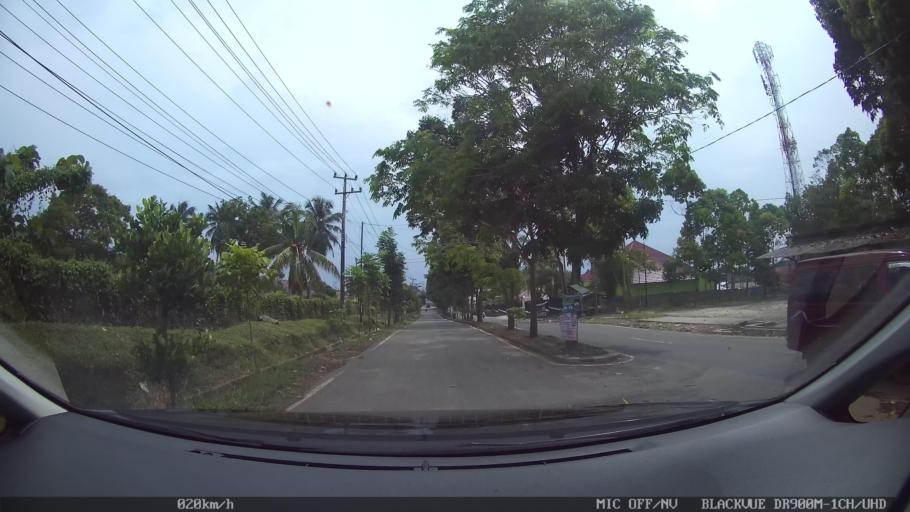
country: ID
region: Lampung
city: Bandarlampung
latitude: -5.4048
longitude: 105.2002
